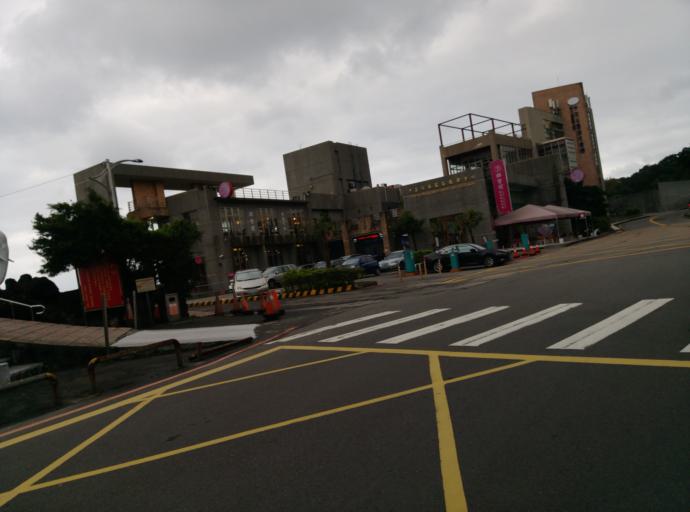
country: TW
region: Taiwan
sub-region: Keelung
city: Keelung
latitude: 25.1331
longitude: 121.7515
